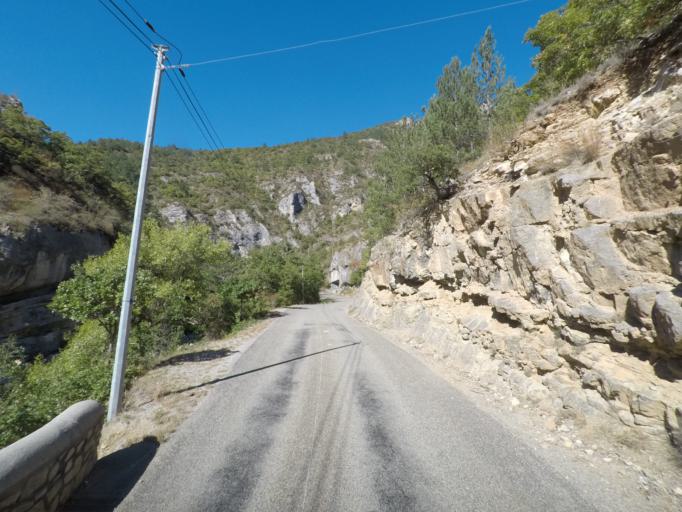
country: FR
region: Rhone-Alpes
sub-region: Departement de la Drome
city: Die
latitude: 44.6392
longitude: 5.2914
